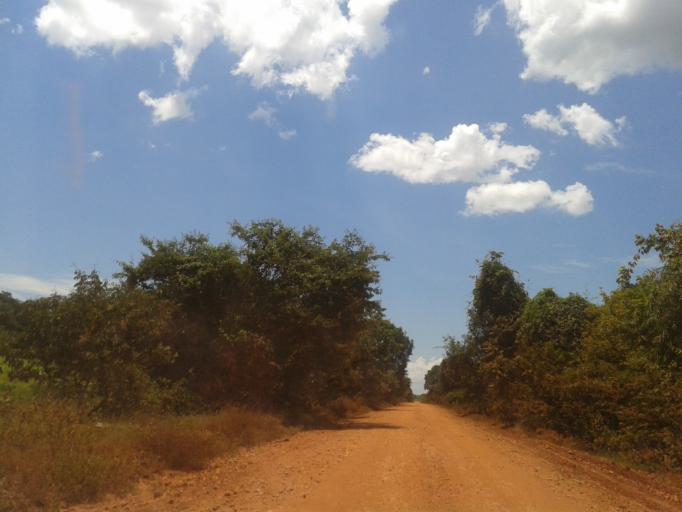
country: BR
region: Minas Gerais
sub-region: Santa Vitoria
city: Santa Vitoria
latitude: -19.1822
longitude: -50.4018
